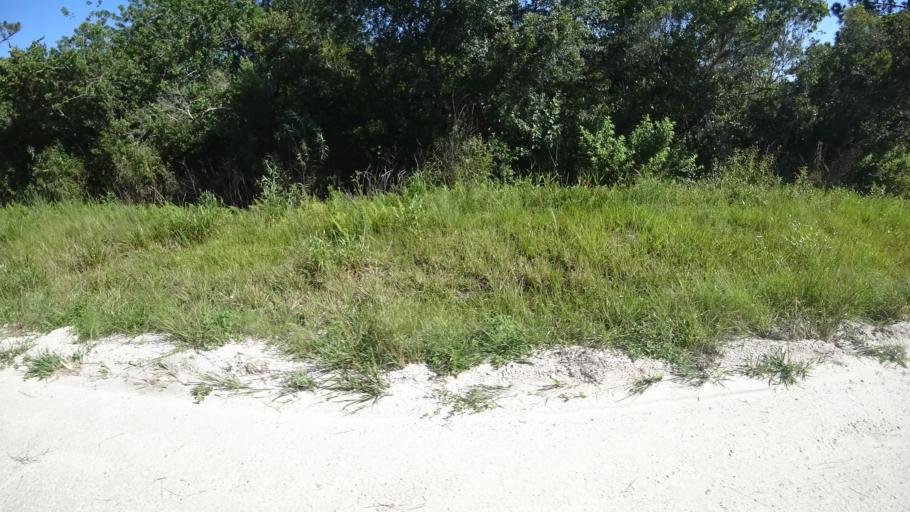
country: US
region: Florida
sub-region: Sarasota County
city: Fruitville
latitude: 27.3978
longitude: -82.2913
